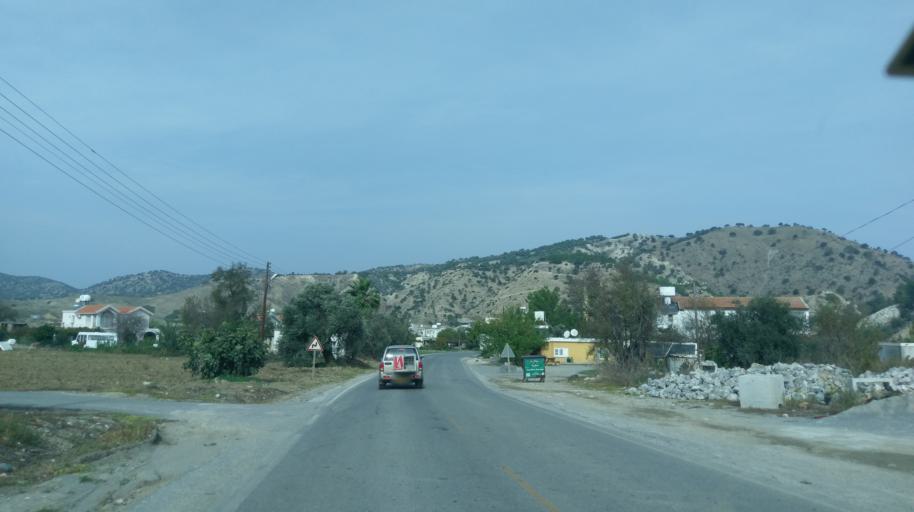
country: CY
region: Keryneia
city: Lapithos
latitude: 35.3334
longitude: 33.0687
